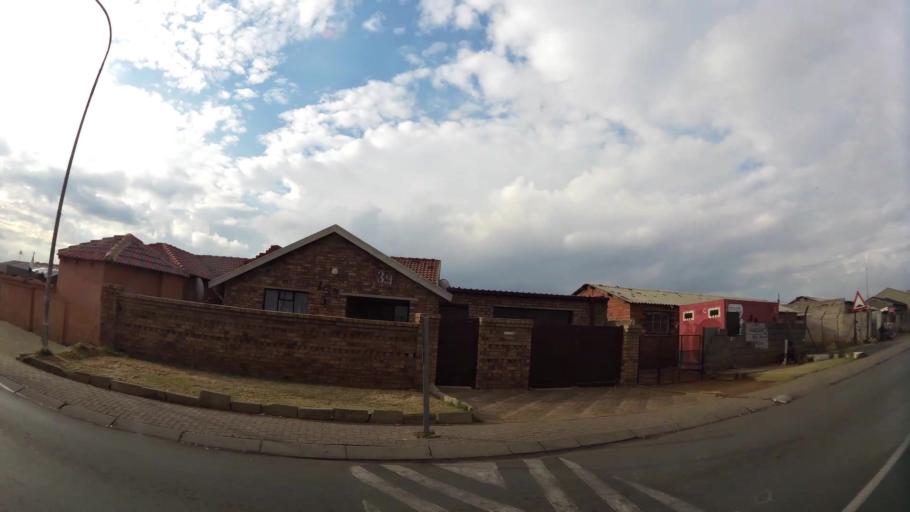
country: ZA
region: Gauteng
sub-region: City of Johannesburg Metropolitan Municipality
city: Soweto
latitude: -26.2522
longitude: 27.8210
